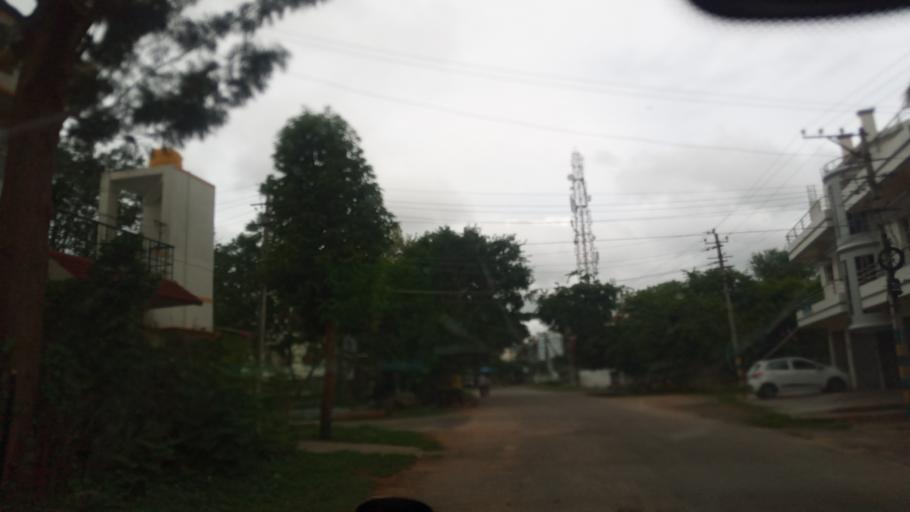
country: IN
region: Karnataka
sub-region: Mysore
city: Mysore
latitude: 12.2872
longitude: 76.6124
